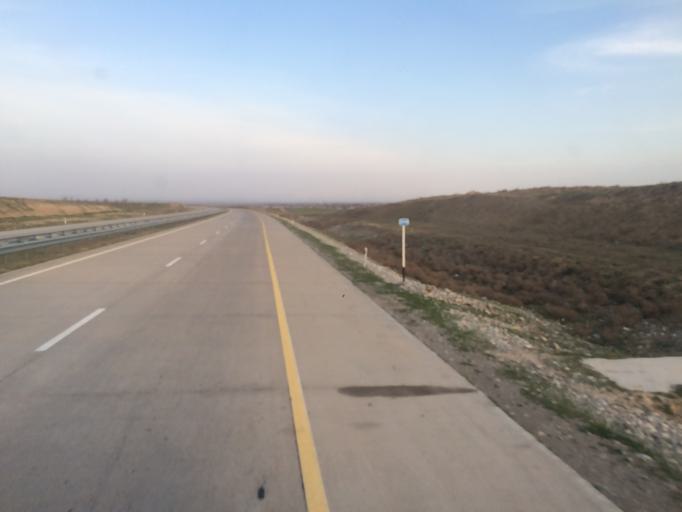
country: KZ
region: Ongtustik Qazaqstan
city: Shymkent
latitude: 42.4932
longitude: 69.4774
